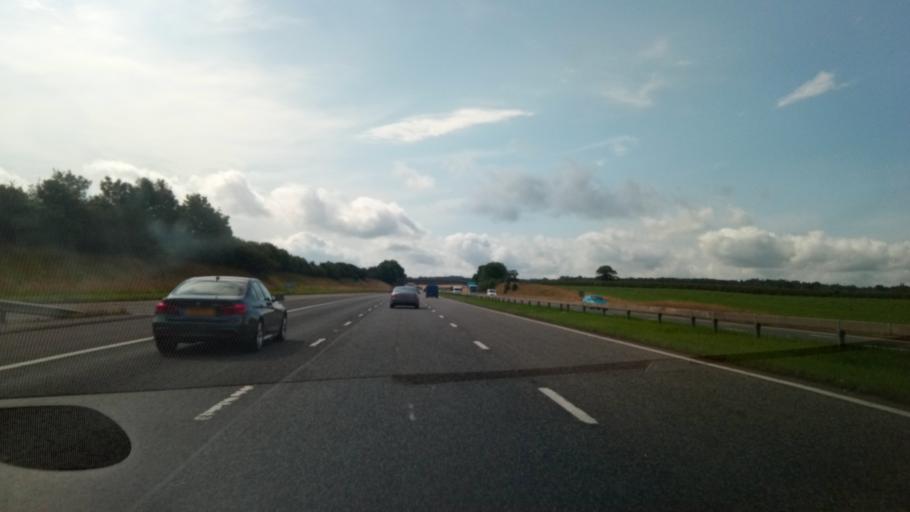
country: GB
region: England
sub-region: Cumbria
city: Penrith
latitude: 54.6265
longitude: -2.7228
